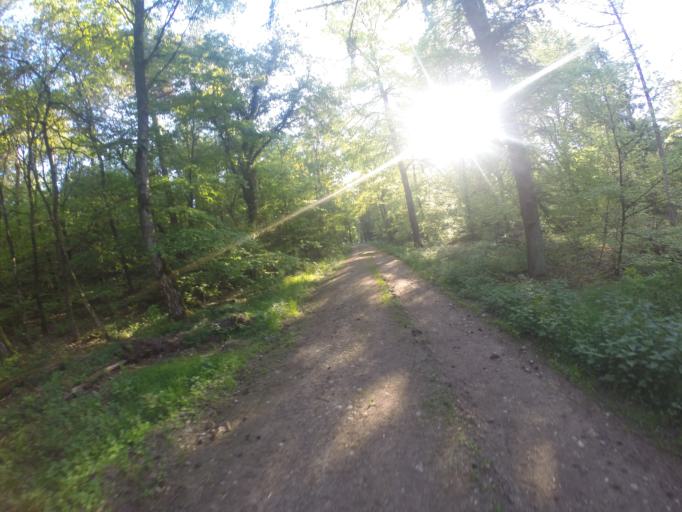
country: NL
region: Gelderland
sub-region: Gemeente Montferland
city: s-Heerenberg
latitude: 51.8972
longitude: 6.2192
